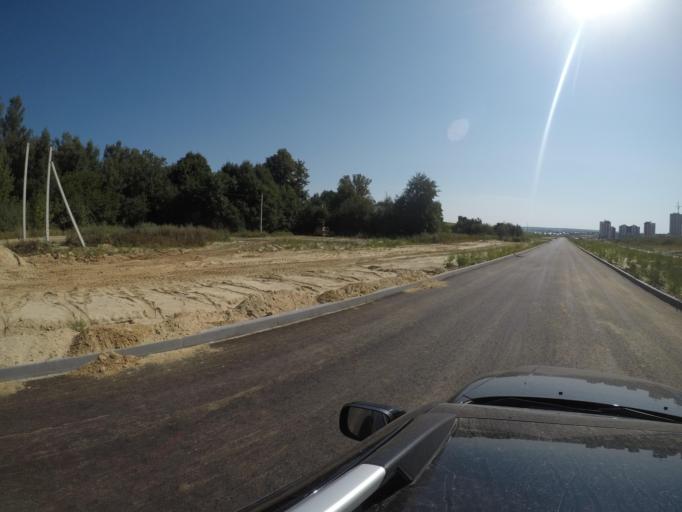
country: BY
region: Grodnenskaya
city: Hrodna
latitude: 53.7269
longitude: 23.8776
